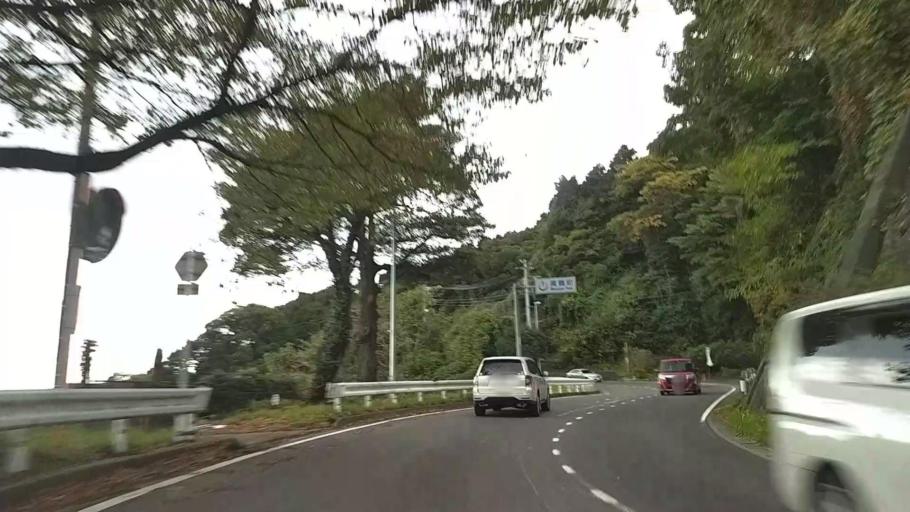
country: JP
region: Kanagawa
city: Yugawara
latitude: 35.1782
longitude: 139.1353
